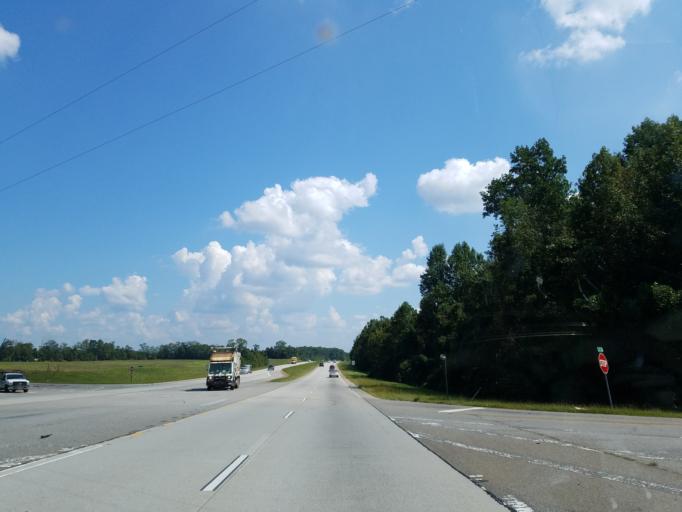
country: US
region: Georgia
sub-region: Oconee County
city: Bogart
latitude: 33.9425
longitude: -83.5635
